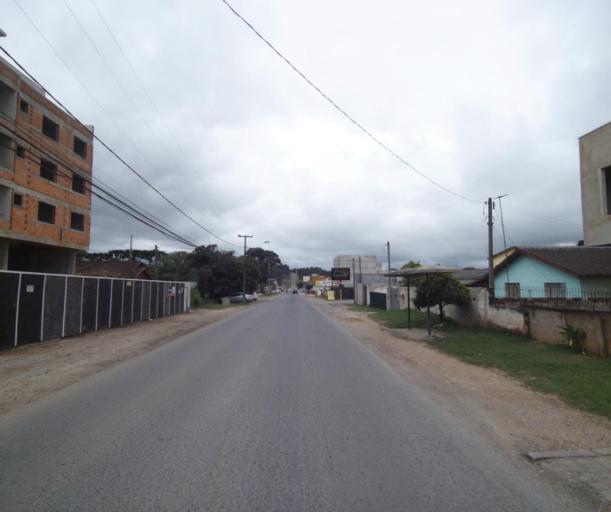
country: BR
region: Parana
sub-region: Quatro Barras
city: Quatro Barras
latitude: -25.3632
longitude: -49.0959
